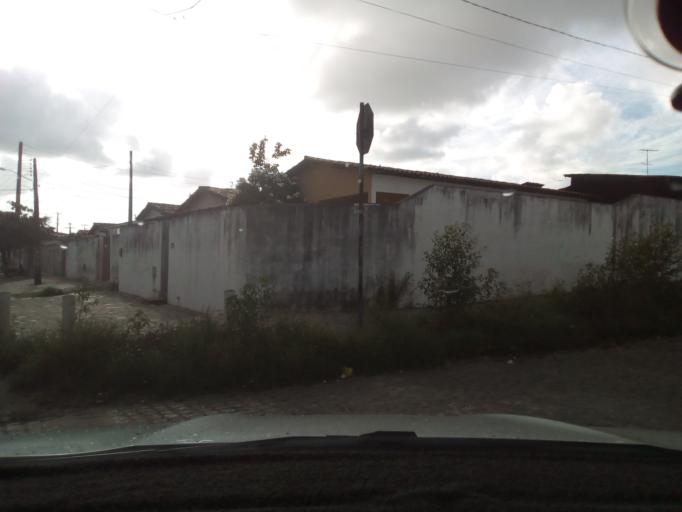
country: BR
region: Paraiba
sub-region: Joao Pessoa
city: Joao Pessoa
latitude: -7.1761
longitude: -34.8879
